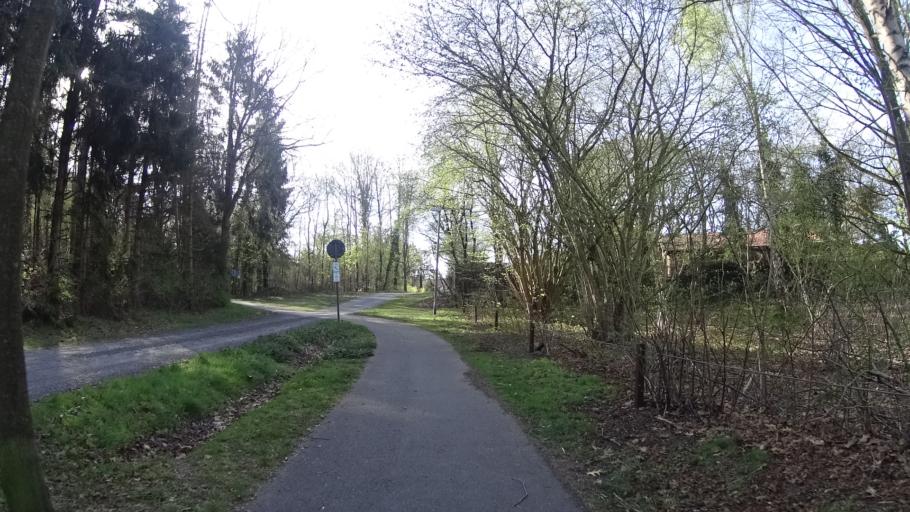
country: DE
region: Lower Saxony
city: Haren
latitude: 52.7916
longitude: 7.2722
